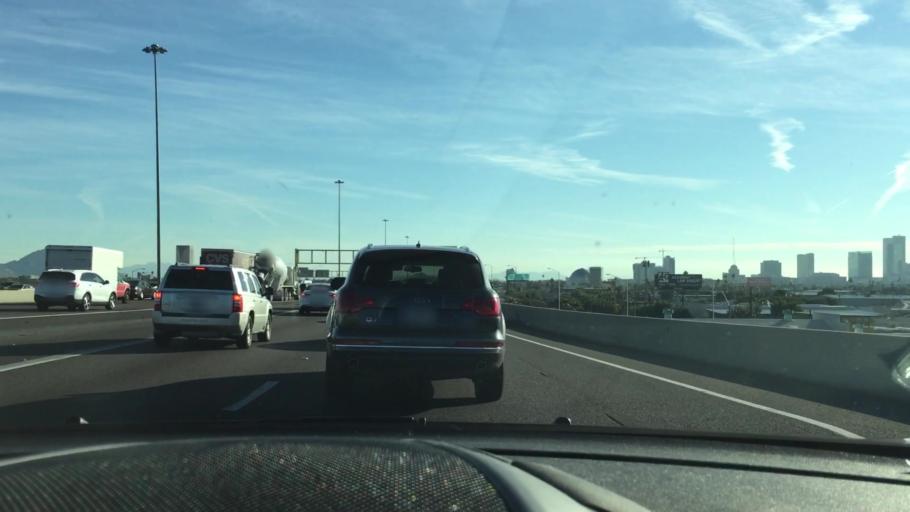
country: US
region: Arizona
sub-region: Maricopa County
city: Phoenix
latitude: 33.4608
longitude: -112.1013
